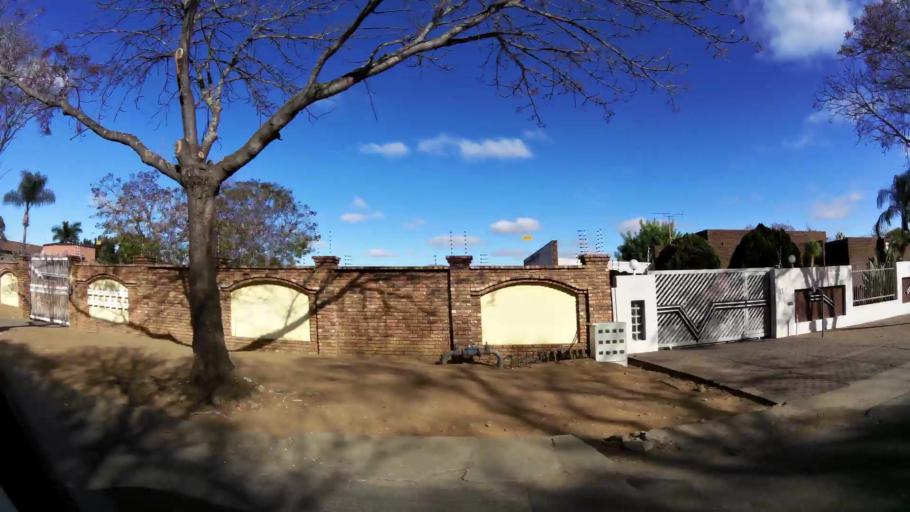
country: ZA
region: Limpopo
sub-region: Capricorn District Municipality
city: Polokwane
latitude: -23.9043
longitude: 29.4587
